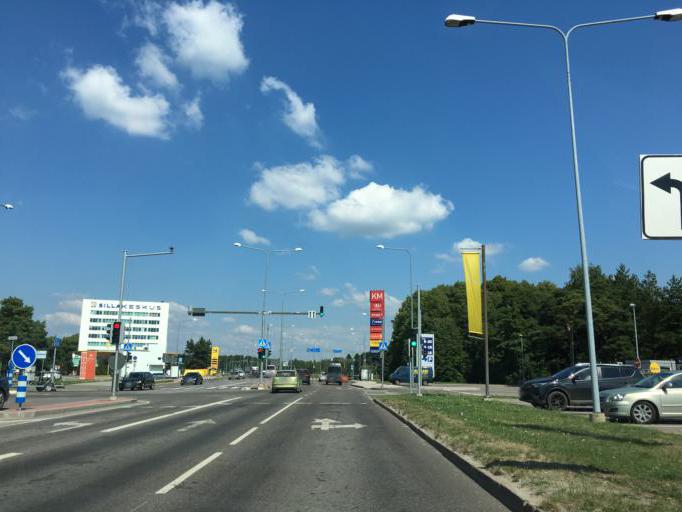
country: EE
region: Paernumaa
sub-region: Paernu linn
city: Parnu
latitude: 58.3730
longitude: 24.5521
